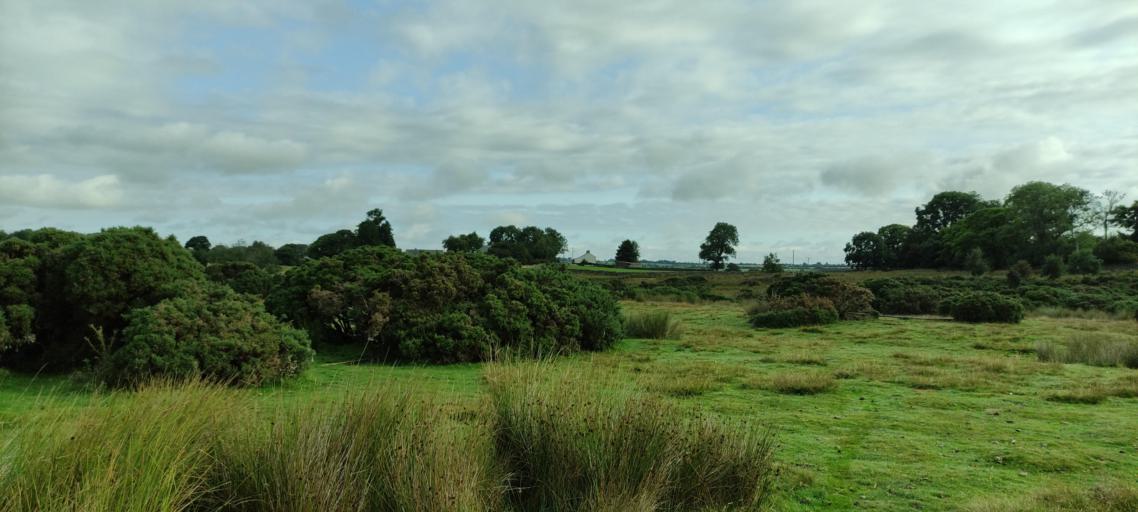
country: GB
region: England
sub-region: Cumbria
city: Keswick
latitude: 54.7079
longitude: -2.9999
